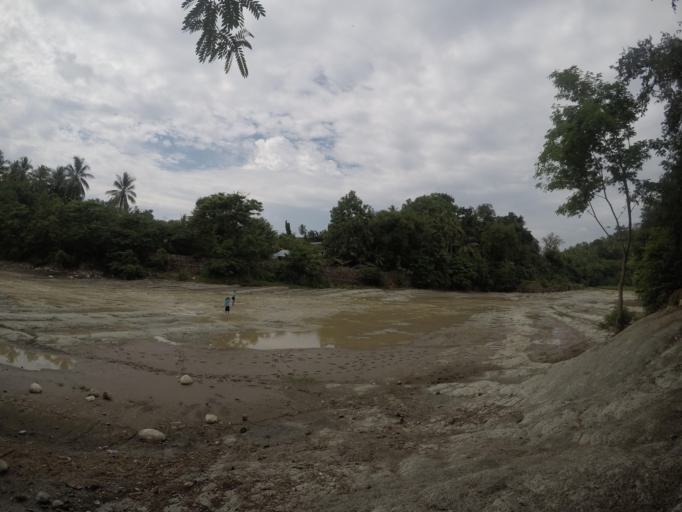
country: TL
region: Viqueque
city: Viqueque
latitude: -8.8648
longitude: 126.3651
